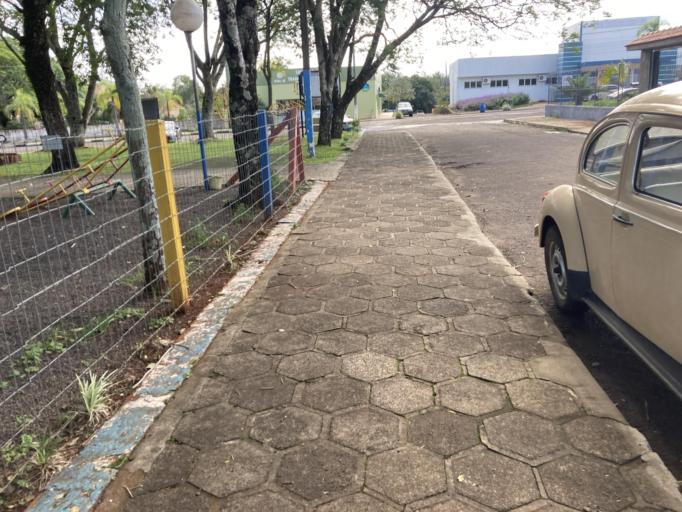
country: BR
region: Rio Grande do Sul
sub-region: Sao Pedro Do Butia
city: Butia Inferior
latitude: -27.9893
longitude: -54.8386
